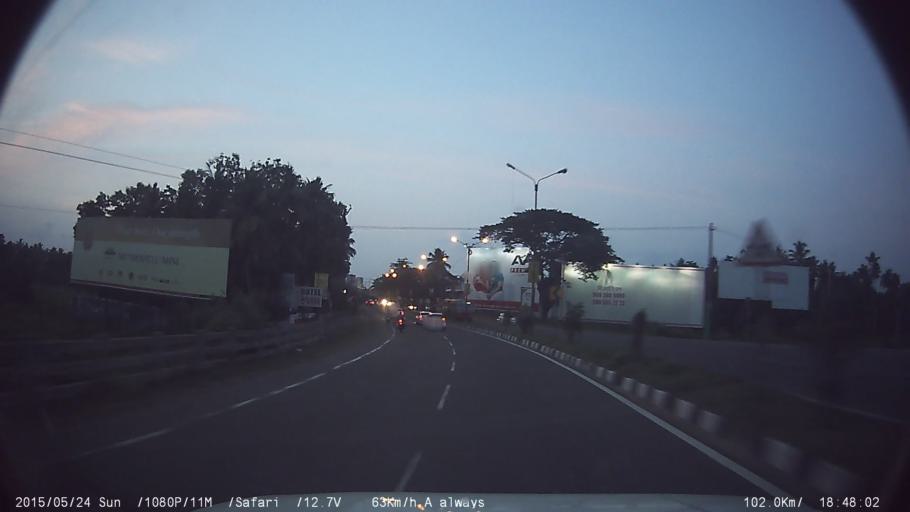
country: IN
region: Kerala
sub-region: Ernakulam
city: Aluva
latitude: 10.1332
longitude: 76.3534
